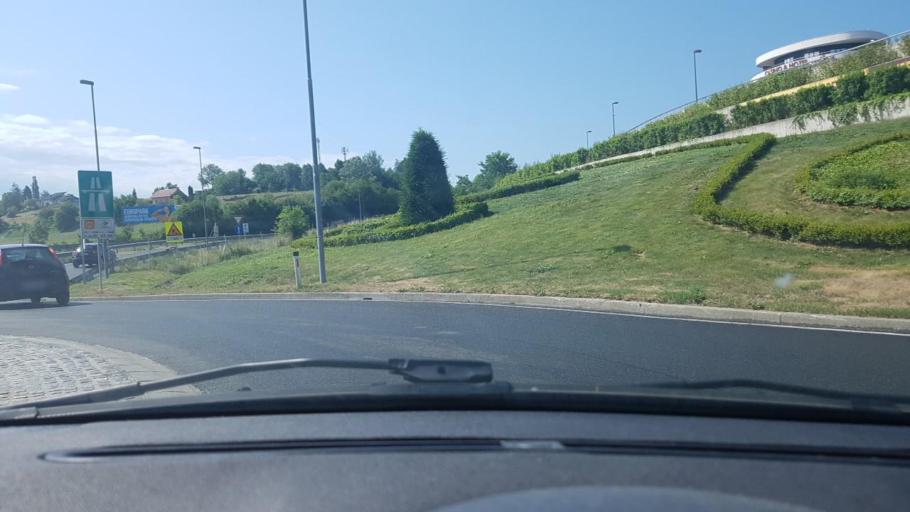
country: SI
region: Sentilj
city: Sentilj v Slov. Goricah
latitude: 46.6783
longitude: 15.6482
